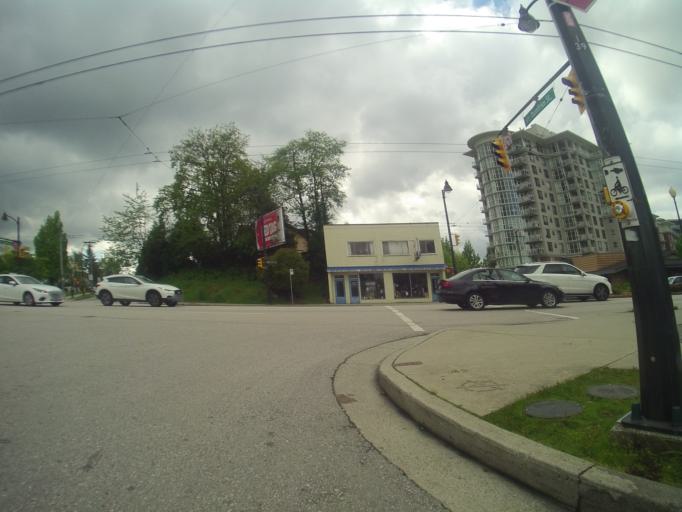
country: CA
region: British Columbia
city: Vancouver
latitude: 49.2493
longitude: -123.0733
